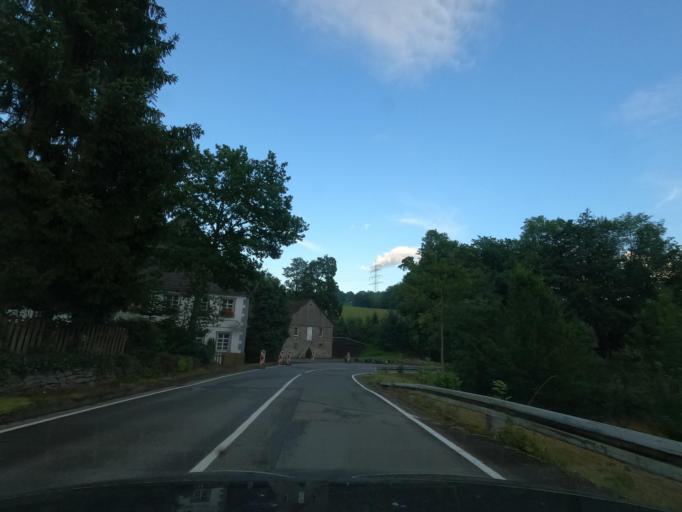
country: DE
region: North Rhine-Westphalia
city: Plettenberg
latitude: 51.2338
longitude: 7.8934
